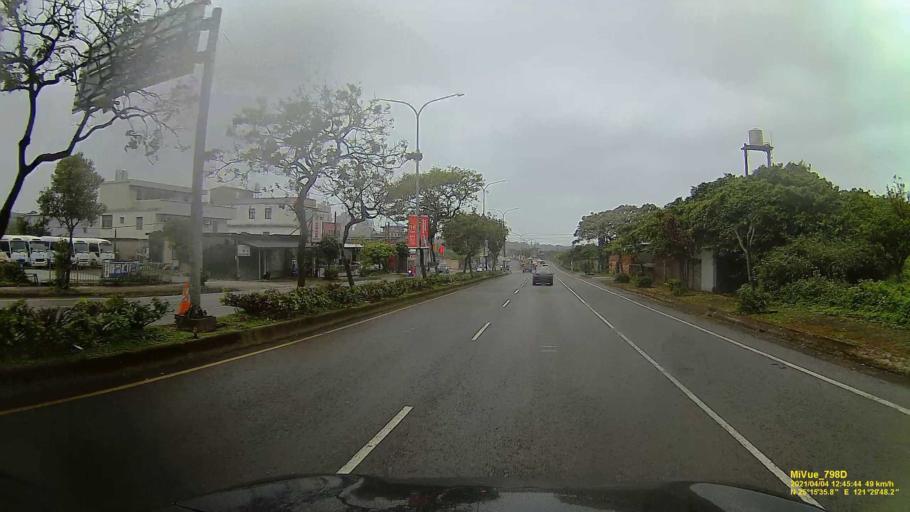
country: TW
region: Taipei
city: Taipei
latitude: 25.2599
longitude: 121.4968
